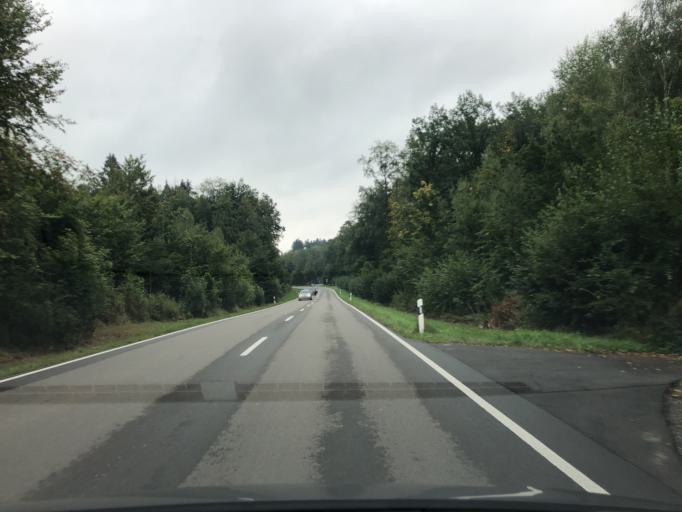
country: DE
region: Baden-Wuerttemberg
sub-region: Regierungsbezirk Stuttgart
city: Gerlingen
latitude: 48.7494
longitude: 9.0538
